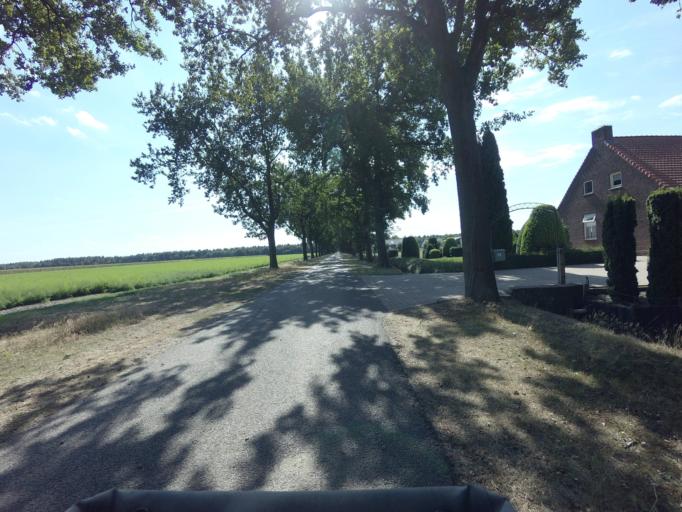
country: NL
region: North Brabant
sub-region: Gemeente Someren
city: Someren
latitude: 51.3460
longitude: 5.6662
